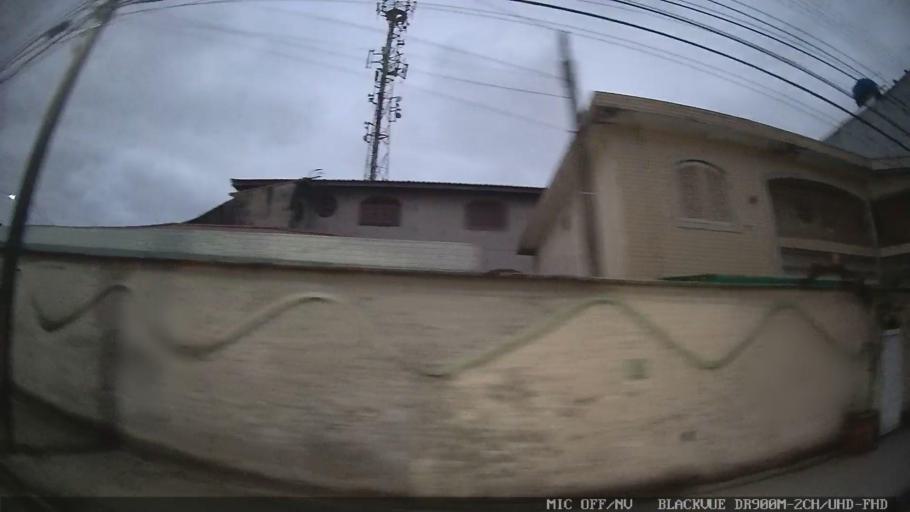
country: BR
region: Sao Paulo
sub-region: Guaruja
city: Guaruja
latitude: -23.9855
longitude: -46.2686
